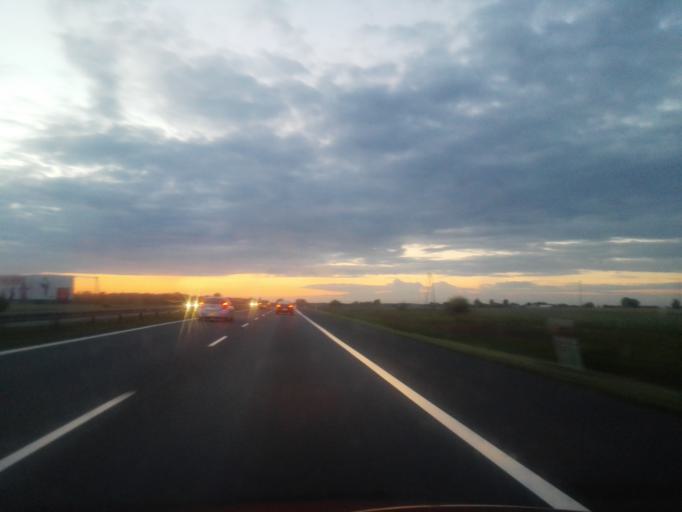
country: PL
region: Lodz Voivodeship
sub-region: Powiat piotrkowski
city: Grabica
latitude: 51.5005
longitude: 19.6069
